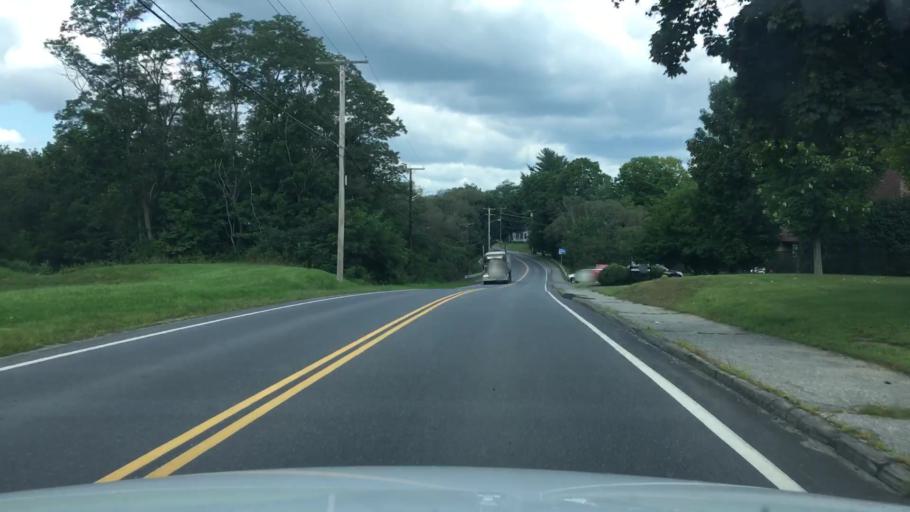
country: US
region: Maine
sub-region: Somerset County
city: Skowhegan
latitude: 44.7586
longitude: -69.7137
